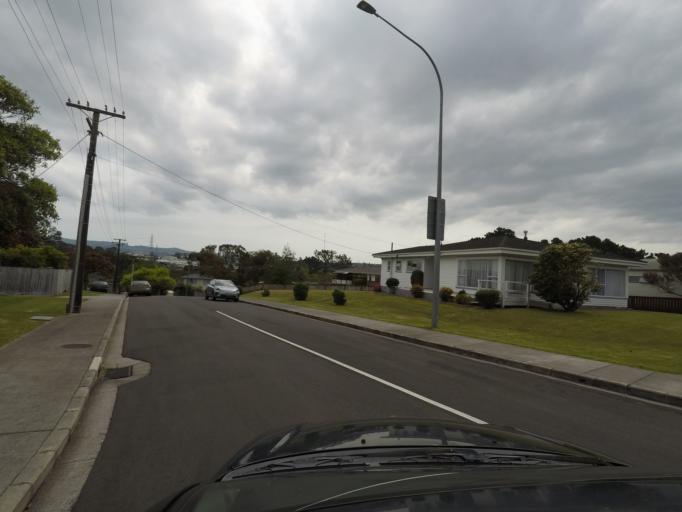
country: NZ
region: Auckland
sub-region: Auckland
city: Rosebank
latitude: -36.8494
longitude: 174.6460
